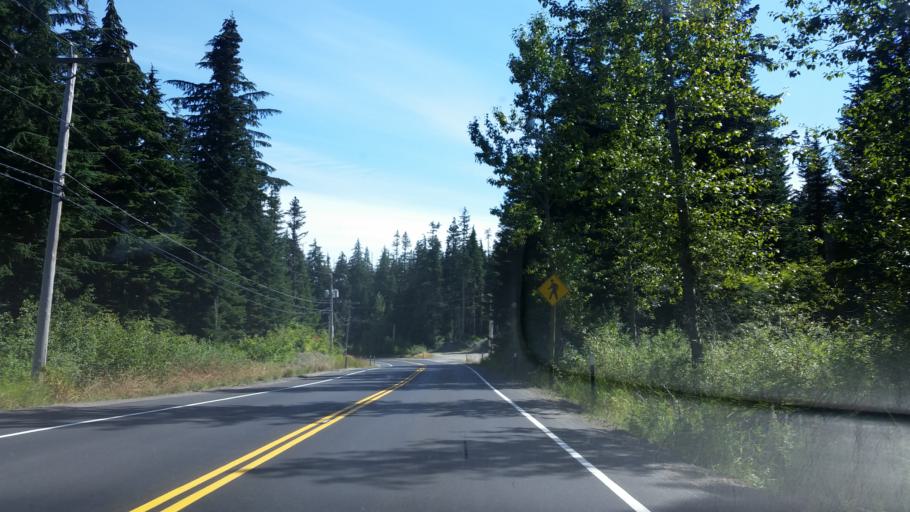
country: US
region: Washington
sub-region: King County
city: Tanner
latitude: 47.4028
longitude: -121.4073
